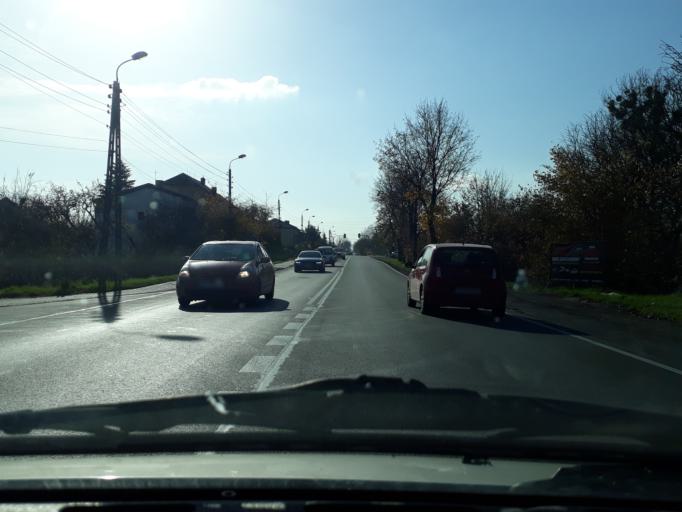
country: PL
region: Silesian Voivodeship
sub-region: Powiat tarnogorski
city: Tarnowskie Gory
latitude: 50.4341
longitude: 18.8441
